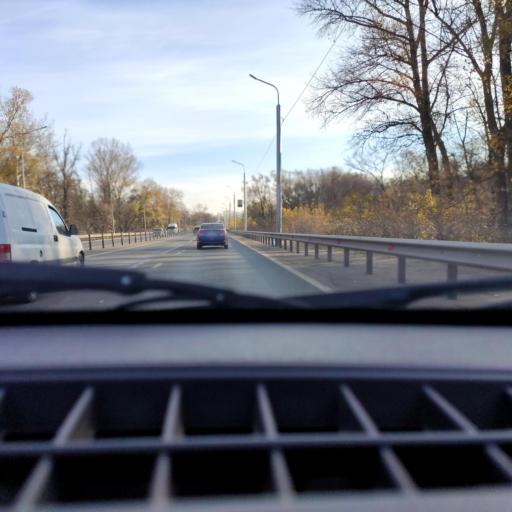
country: RU
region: Bashkortostan
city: Ufa
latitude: 54.6998
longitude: 55.9049
